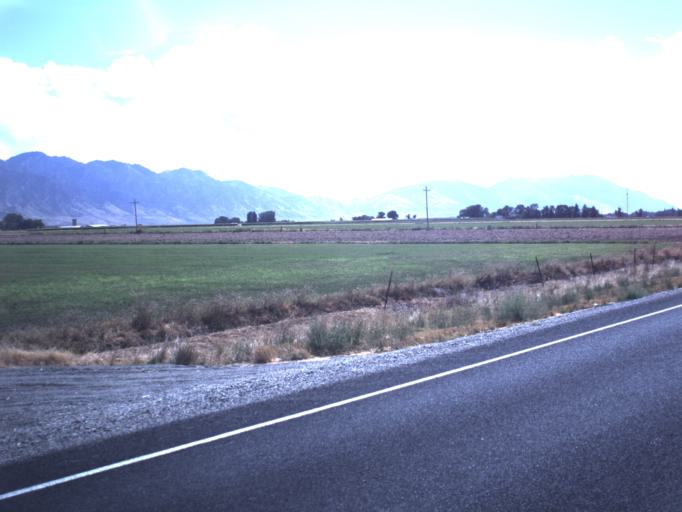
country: US
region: Utah
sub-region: Box Elder County
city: Elwood
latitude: 41.6567
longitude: -112.1404
